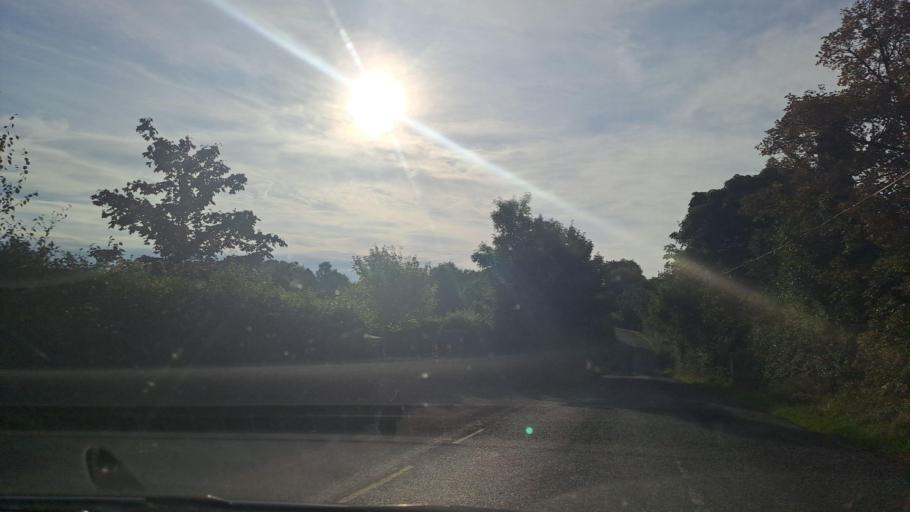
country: IE
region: Ulster
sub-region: An Cabhan
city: Kingscourt
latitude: 53.9610
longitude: -6.8508
